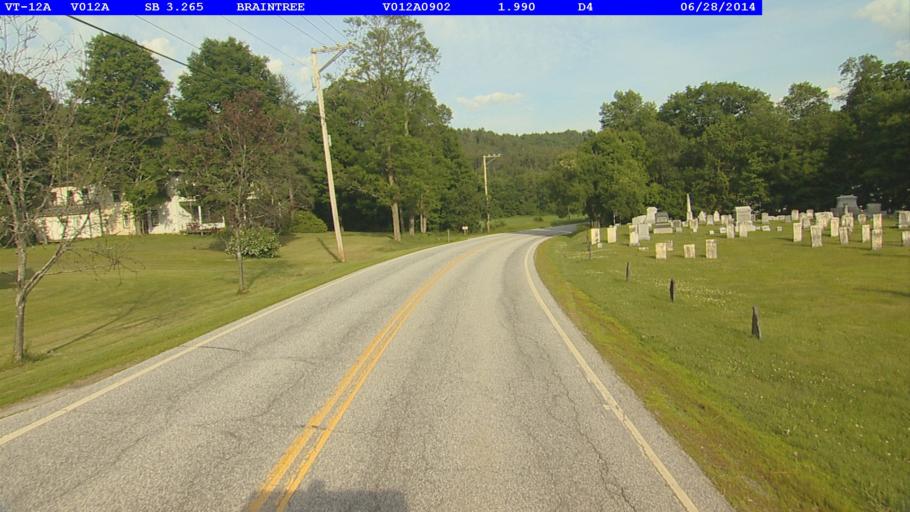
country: US
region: Vermont
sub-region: Orange County
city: Randolph
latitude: 43.9489
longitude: -72.7124
